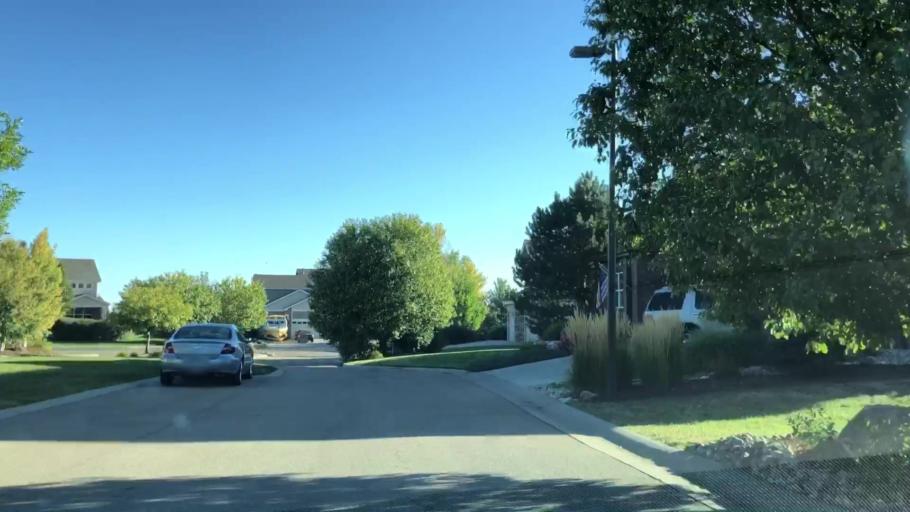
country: US
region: Colorado
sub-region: Larimer County
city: Loveland
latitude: 40.4604
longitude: -105.0339
